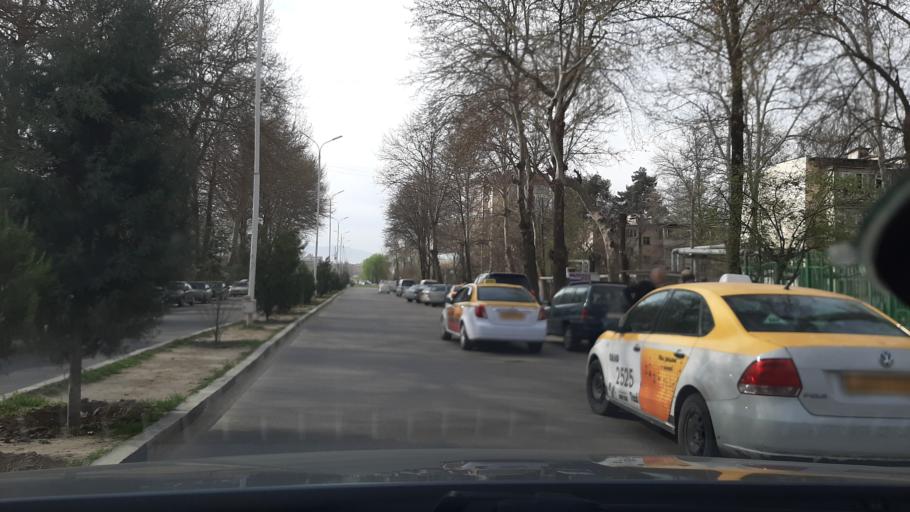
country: TJ
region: Dushanbe
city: Dushanbe
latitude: 38.5800
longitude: 68.7490
